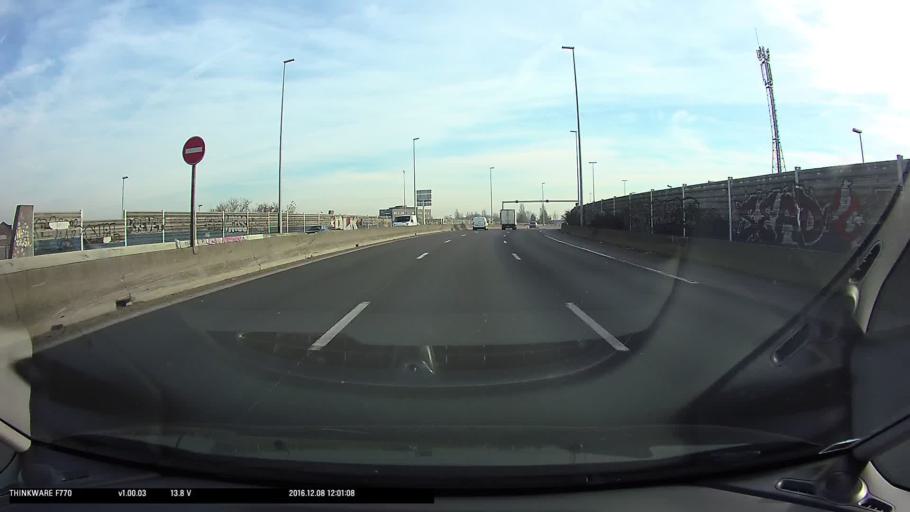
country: FR
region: Ile-de-France
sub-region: Departement de Seine-Saint-Denis
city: La Courneuve
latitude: 48.9284
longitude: 2.4139
